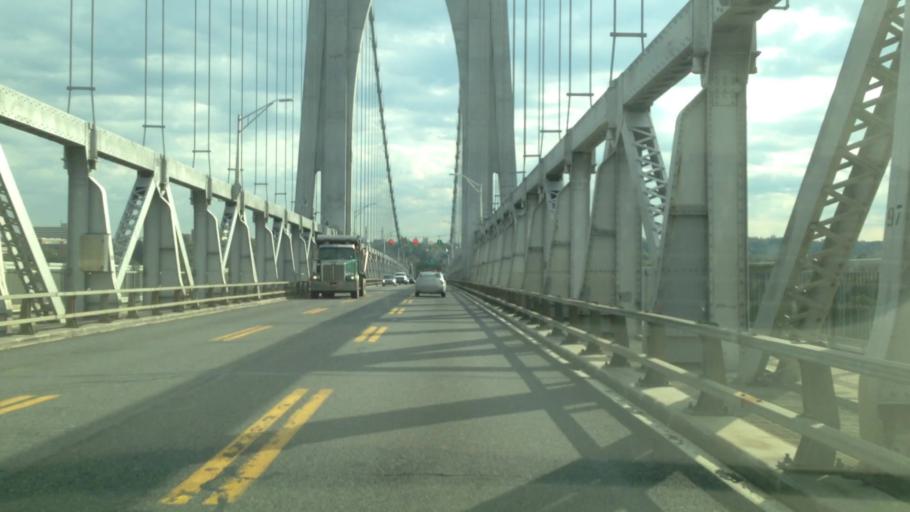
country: US
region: New York
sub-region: Dutchess County
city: Poughkeepsie
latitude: 41.7028
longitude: -73.9428
